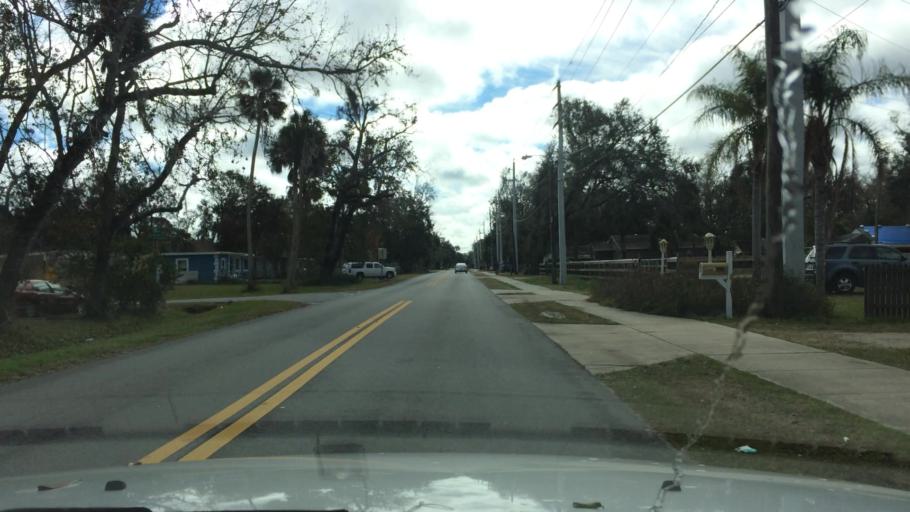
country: US
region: Florida
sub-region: Volusia County
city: Holly Hill
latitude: 29.2320
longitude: -81.0446
